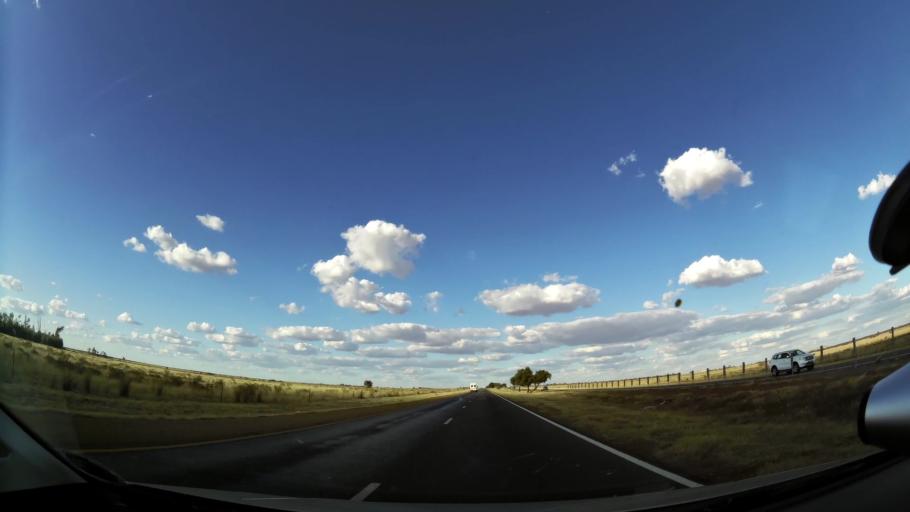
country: ZA
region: North-West
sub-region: Dr Kenneth Kaunda District Municipality
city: Klerksdorp
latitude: -26.8467
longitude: 26.7139
